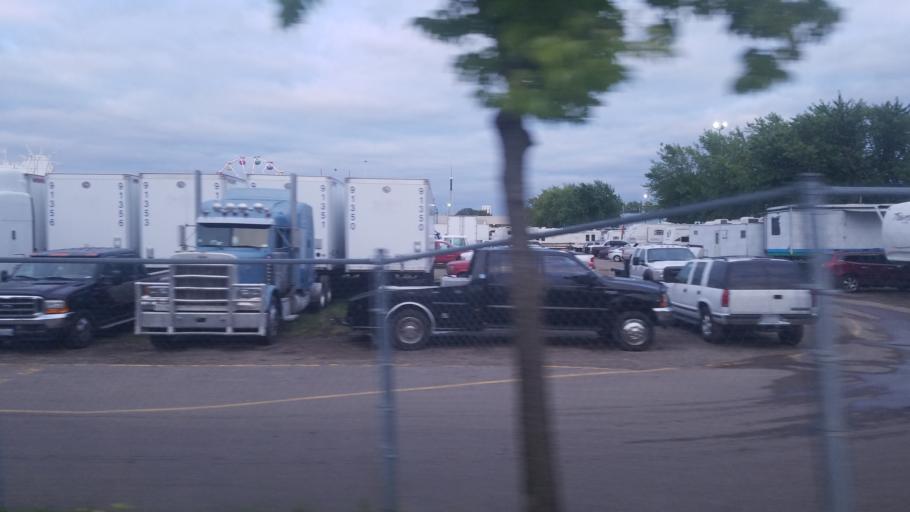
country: US
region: Minnesota
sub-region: Ramsey County
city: Falcon Heights
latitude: 44.9795
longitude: -93.1809
